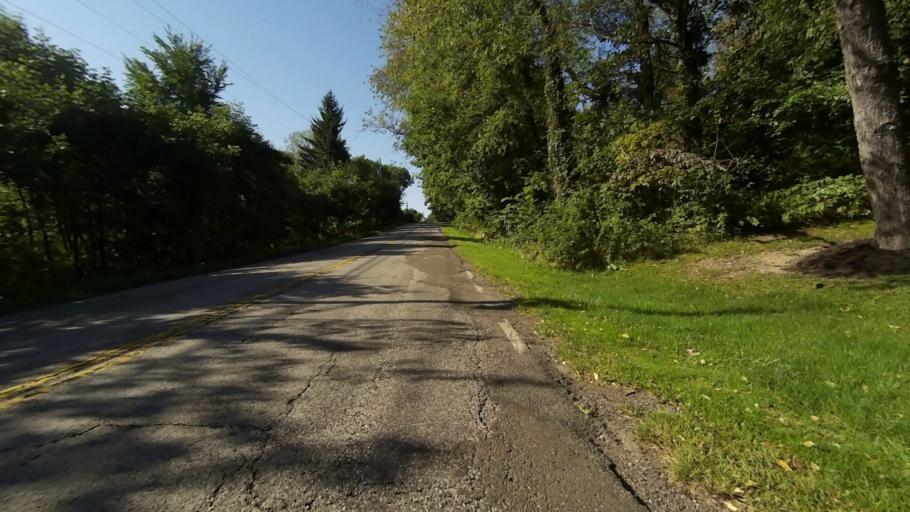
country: US
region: Ohio
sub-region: Portage County
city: Streetsboro
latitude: 41.2352
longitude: -81.3069
